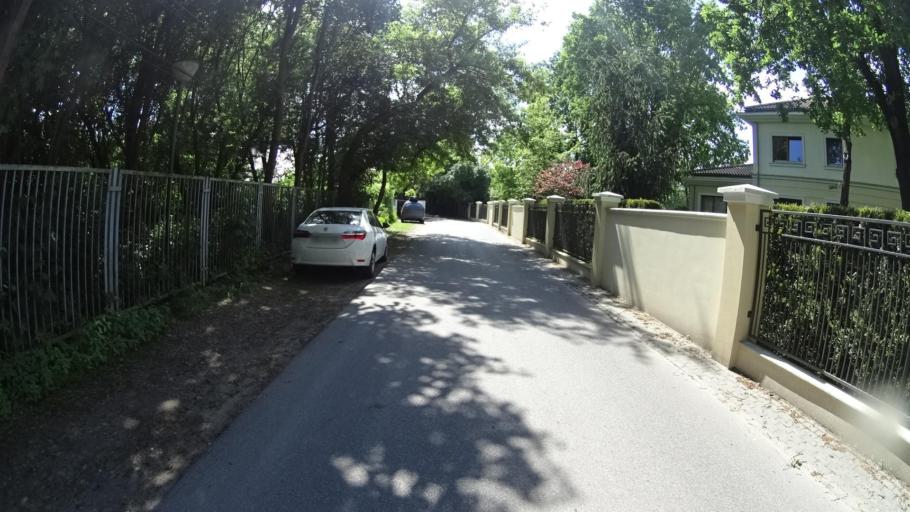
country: PL
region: Masovian Voivodeship
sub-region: Powiat piaseczynski
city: Konstancin-Jeziorna
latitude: 52.1008
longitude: 21.1073
